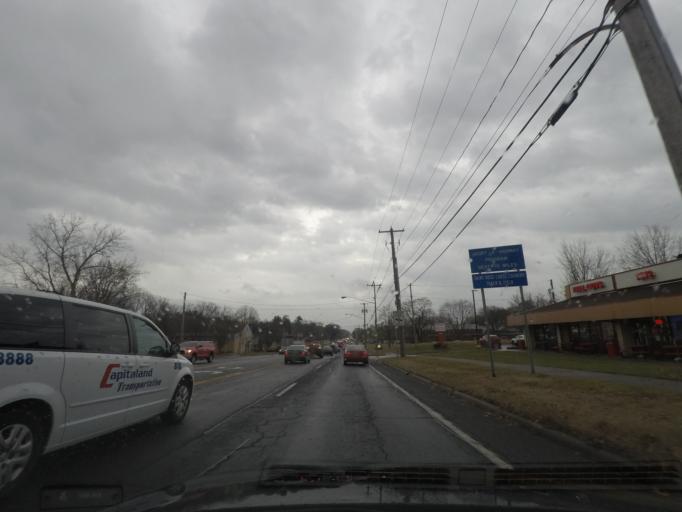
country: US
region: New York
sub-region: Albany County
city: McKownville
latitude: 42.6826
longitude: -73.8425
